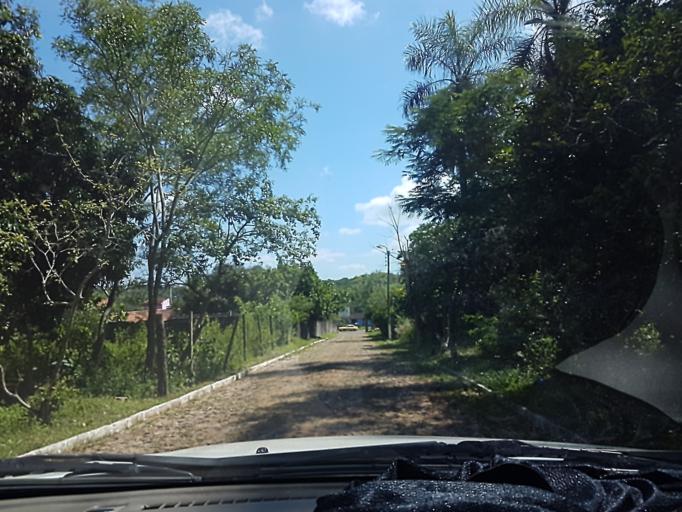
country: PY
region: Central
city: Limpio
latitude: -25.2369
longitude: -57.4442
